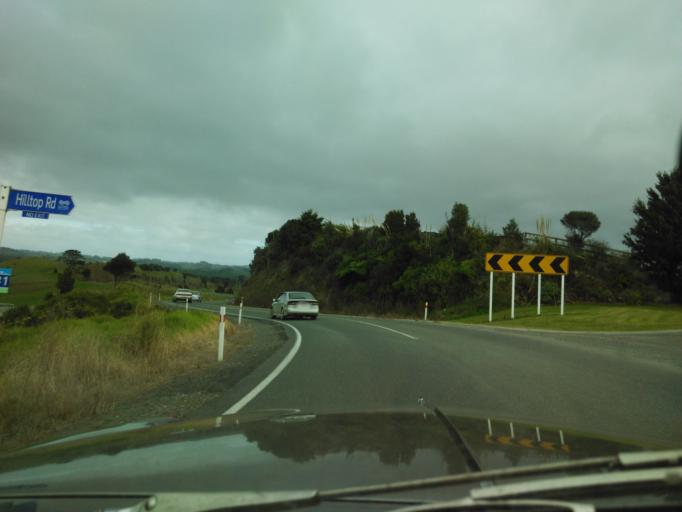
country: NZ
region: Auckland
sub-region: Auckland
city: Wellsford
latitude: -36.1323
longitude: 174.5295
